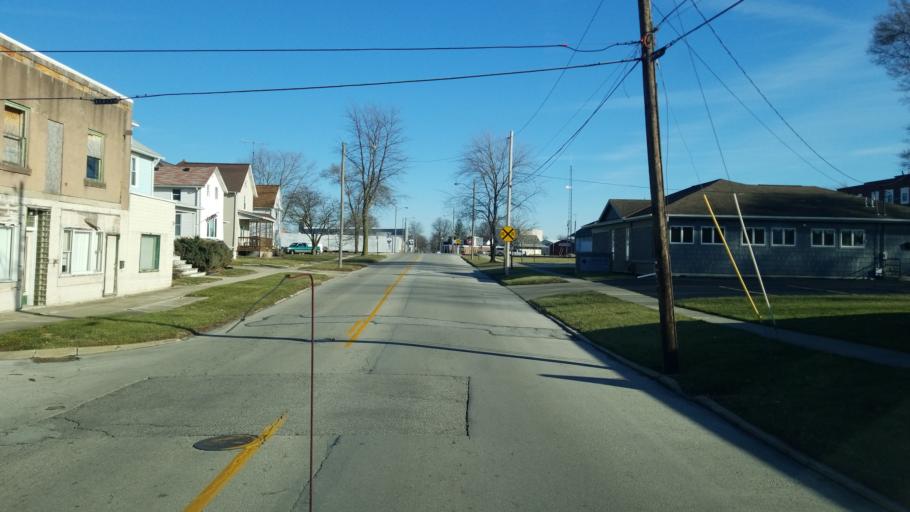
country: US
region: Ohio
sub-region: Sandusky County
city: Fremont
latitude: 41.3485
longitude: -83.1288
